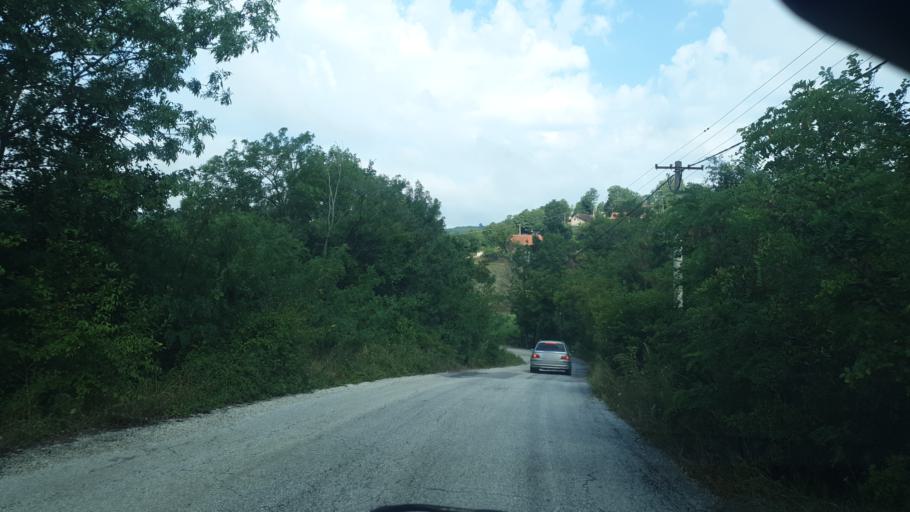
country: RS
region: Central Serbia
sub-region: Sumadijski Okrug
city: Kragujevac
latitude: 44.1044
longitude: 20.7889
